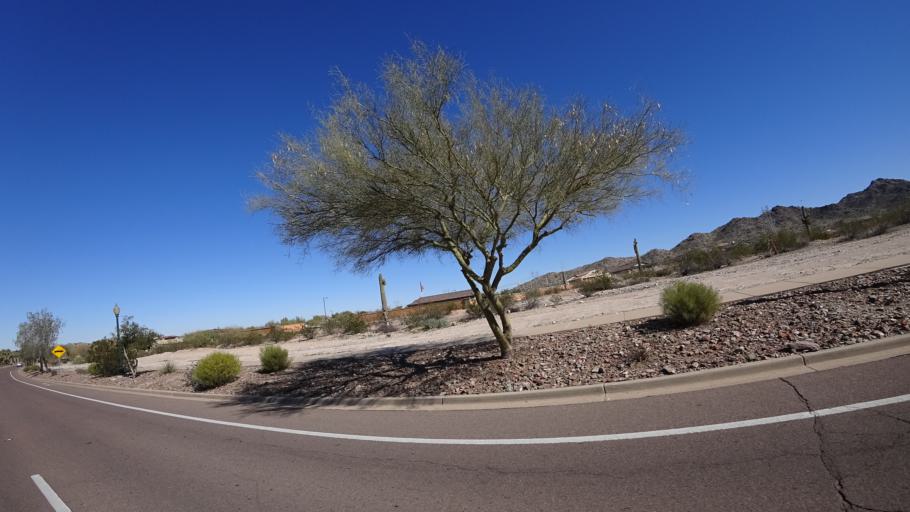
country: US
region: Arizona
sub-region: Maricopa County
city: Goodyear
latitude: 33.3476
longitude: -112.4275
